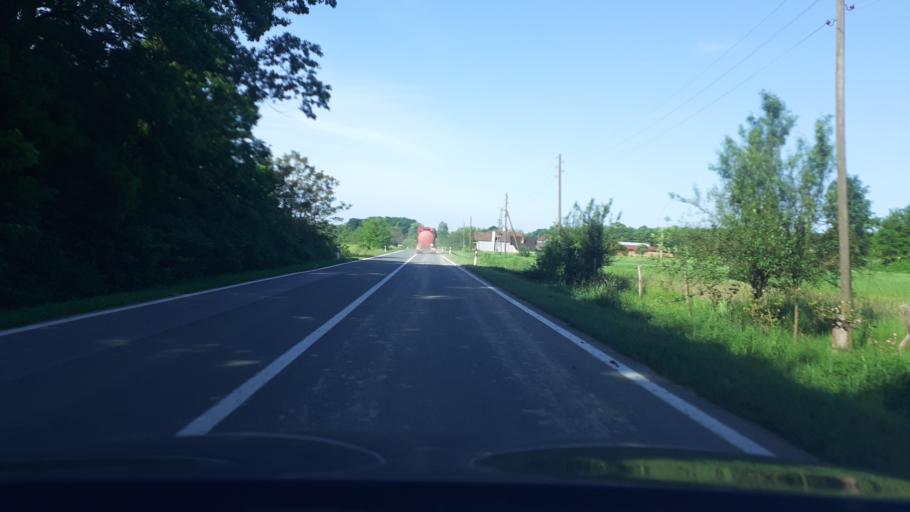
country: HR
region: Brodsko-Posavska
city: Batrina
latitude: 45.2033
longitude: 17.6747
